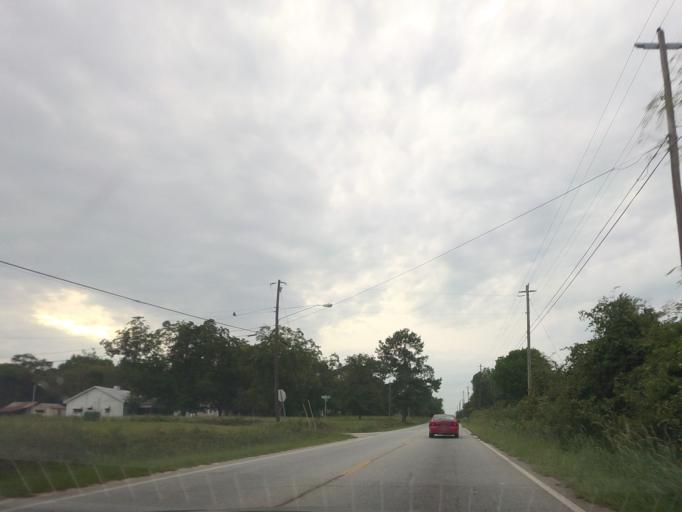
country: US
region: Georgia
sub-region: Bibb County
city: Macon
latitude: 32.8096
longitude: -83.5133
